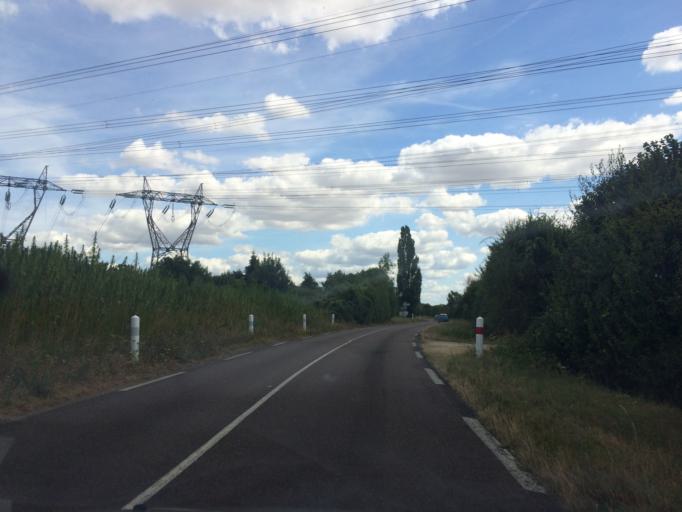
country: FR
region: Ile-de-France
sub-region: Departement de l'Essonne
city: Leudeville
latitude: 48.5514
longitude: 2.3147
